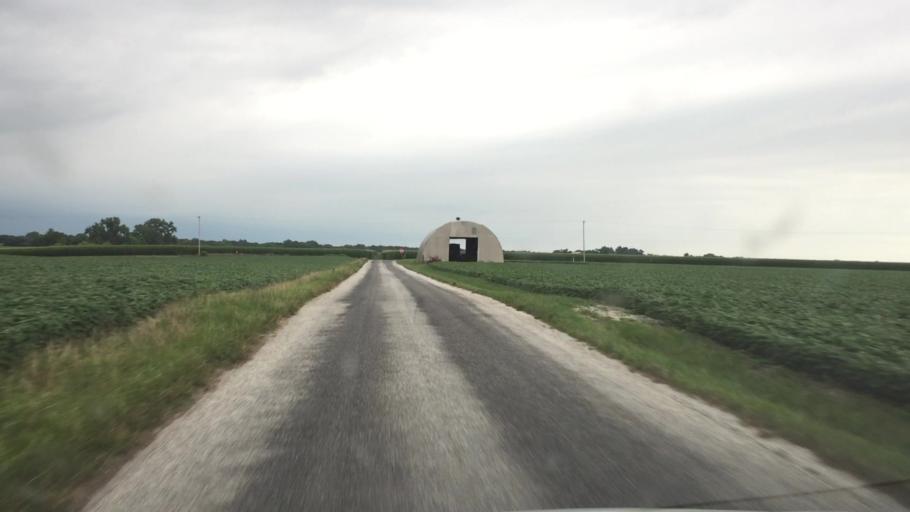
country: US
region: Illinois
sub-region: Adams County
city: Camp Point
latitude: 40.2283
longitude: -90.9690
